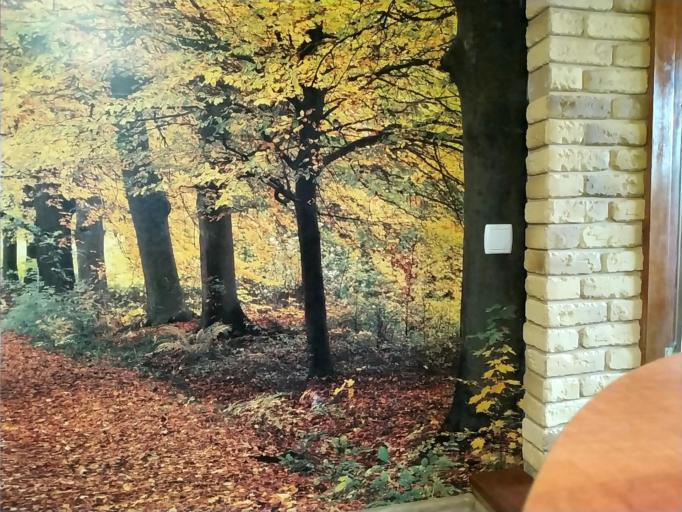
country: RU
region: Leningrad
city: Tolmachevo
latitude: 58.9387
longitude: 29.6826
